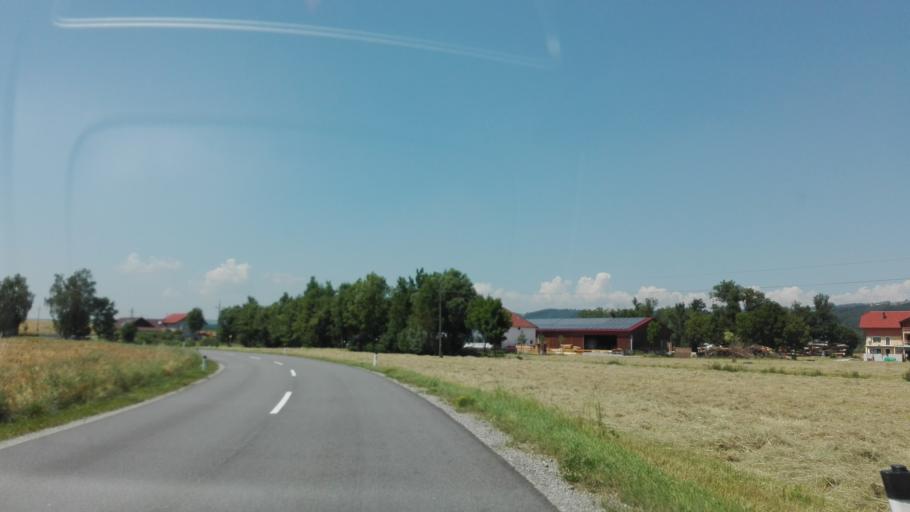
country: AT
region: Upper Austria
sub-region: Politischer Bezirk Grieskirchen
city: Grieskirchen
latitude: 48.3452
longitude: 13.8713
